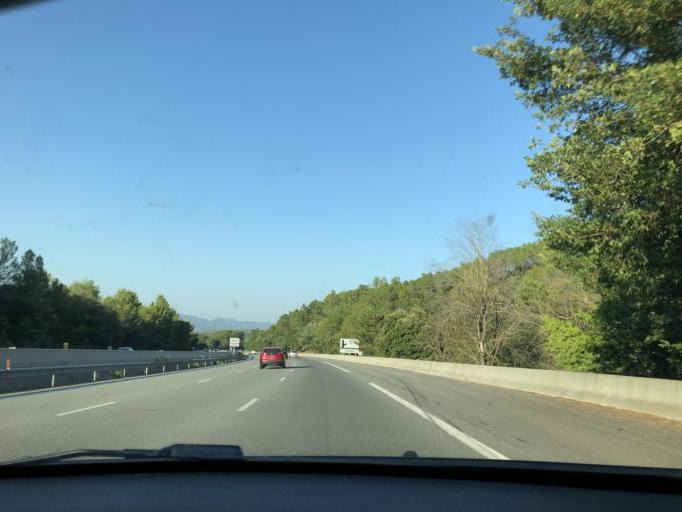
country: FR
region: Provence-Alpes-Cote d'Azur
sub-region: Departement du Var
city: La Motte
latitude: 43.4524
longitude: 6.5223
